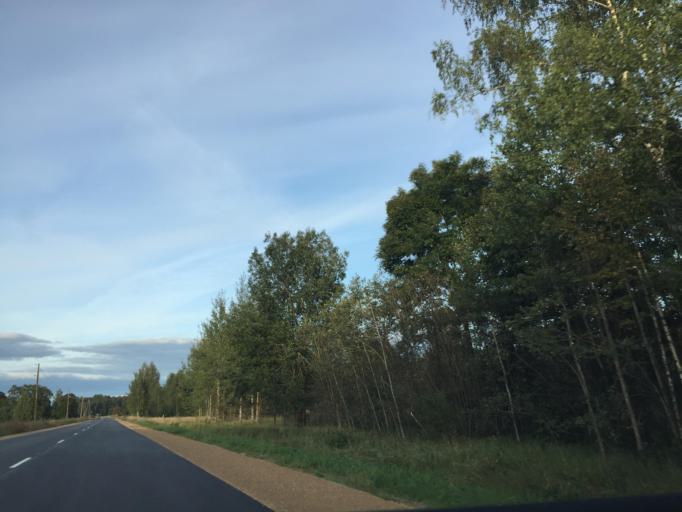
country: LV
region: Viesite
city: Viesite
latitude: 56.3610
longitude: 25.6194
